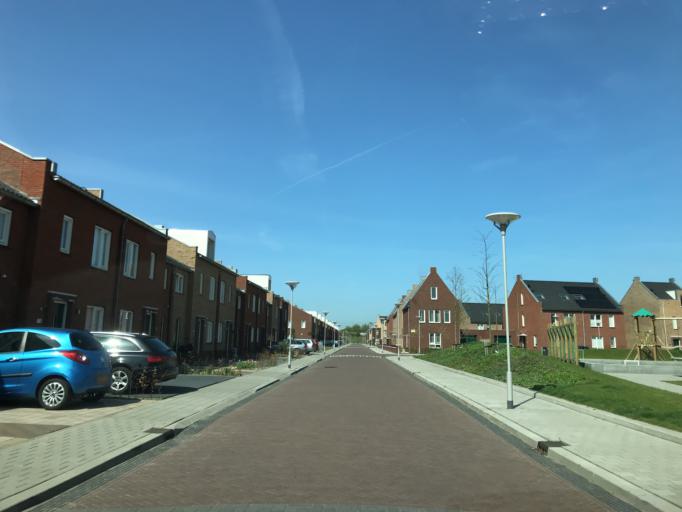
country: NL
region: North Holland
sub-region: Gemeente Diemen
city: Diemen
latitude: 52.3341
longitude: 4.9719
